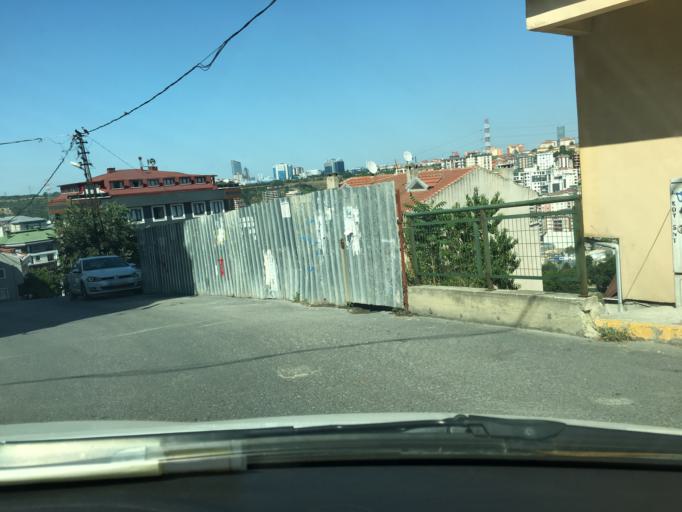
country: TR
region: Istanbul
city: Sisli
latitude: 41.0793
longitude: 28.9457
